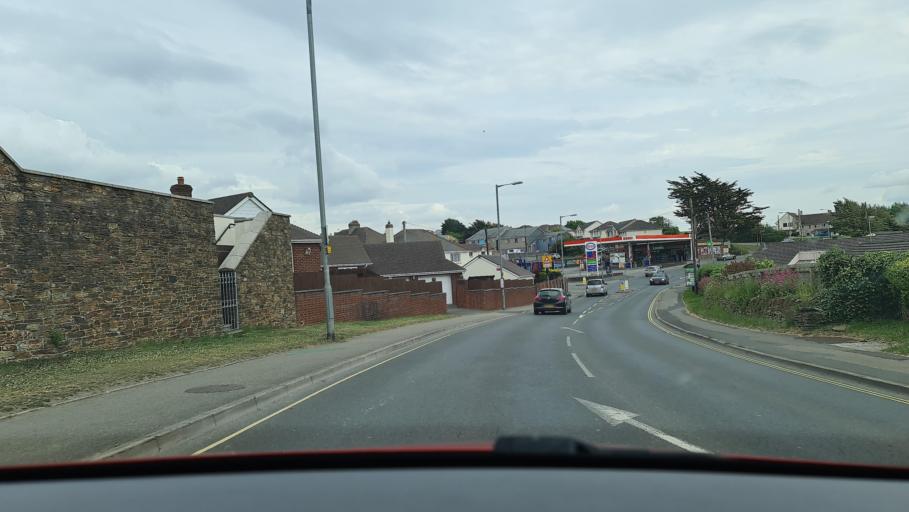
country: GB
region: England
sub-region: Cornwall
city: Bude
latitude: 50.8259
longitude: -4.5425
